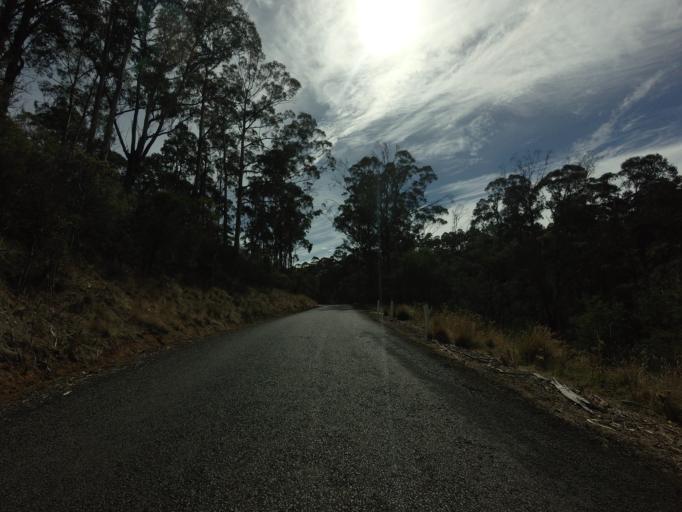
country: AU
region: Tasmania
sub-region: Sorell
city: Sorell
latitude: -42.5633
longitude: 147.6816
